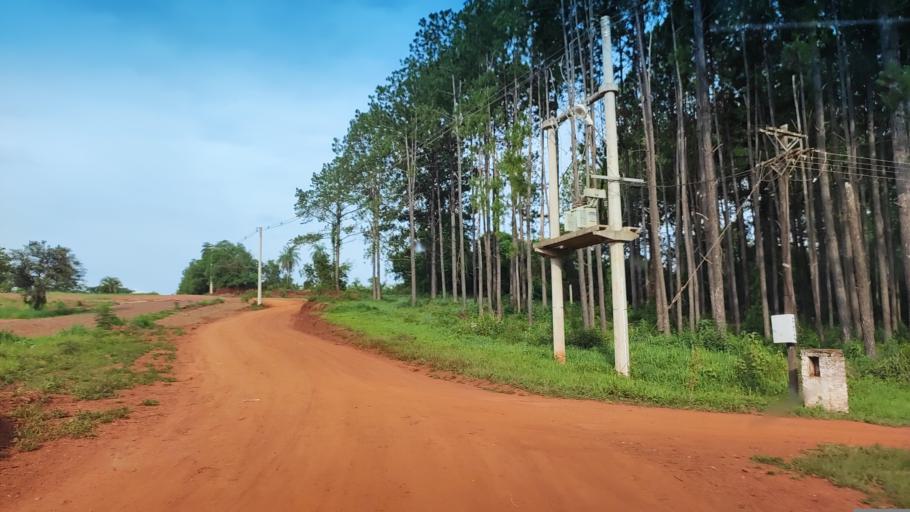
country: AR
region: Misiones
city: Gobernador Roca
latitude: -27.1370
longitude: -55.5190
